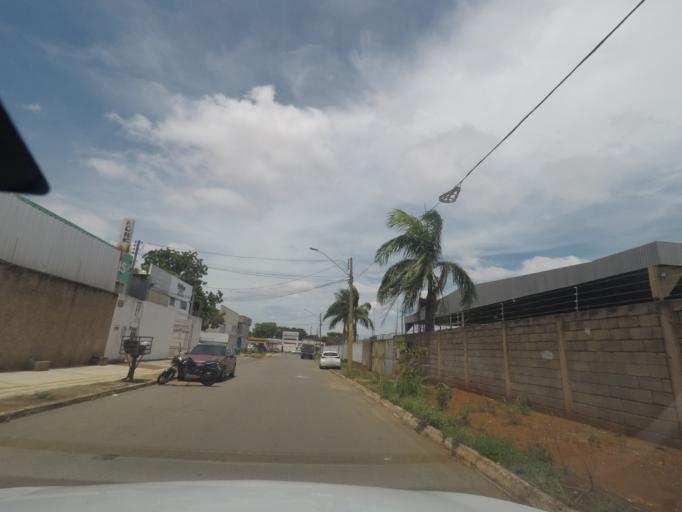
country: BR
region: Goias
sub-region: Goiania
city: Goiania
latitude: -16.6301
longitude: -49.2316
